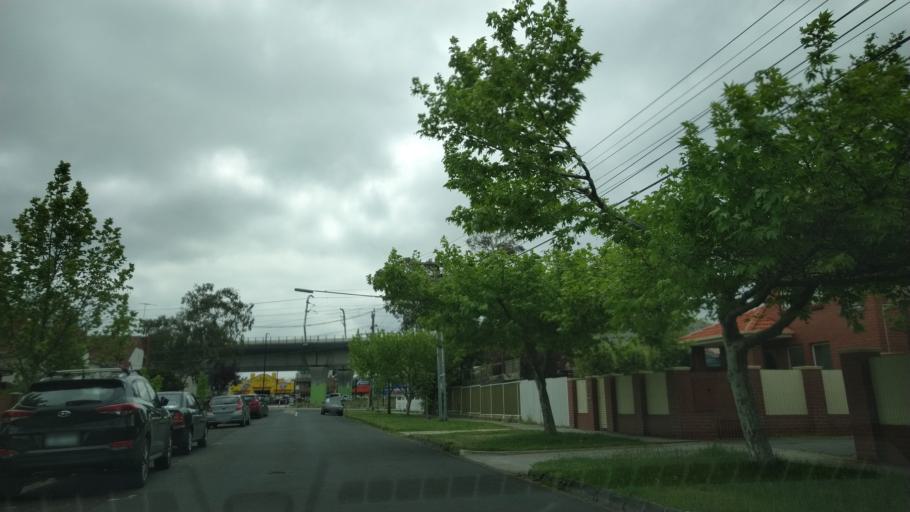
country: AU
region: Victoria
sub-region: Glen Eira
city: Murrumbeena
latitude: -37.8920
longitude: 145.0686
